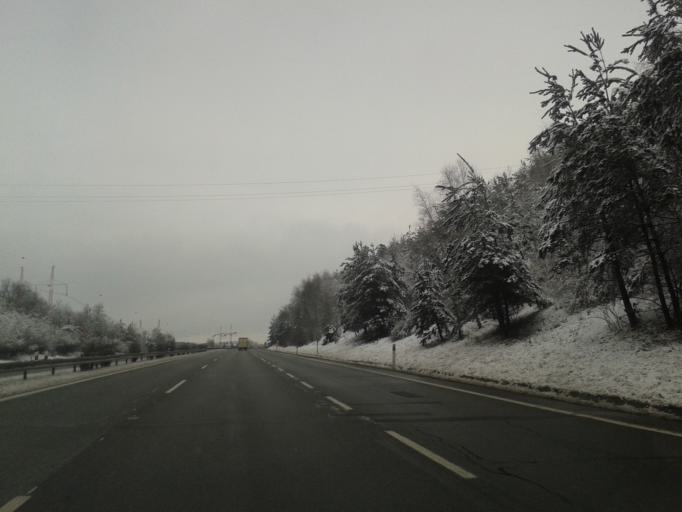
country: CZ
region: Central Bohemia
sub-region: Okres Beroun
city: Beroun
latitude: 49.9715
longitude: 14.1026
